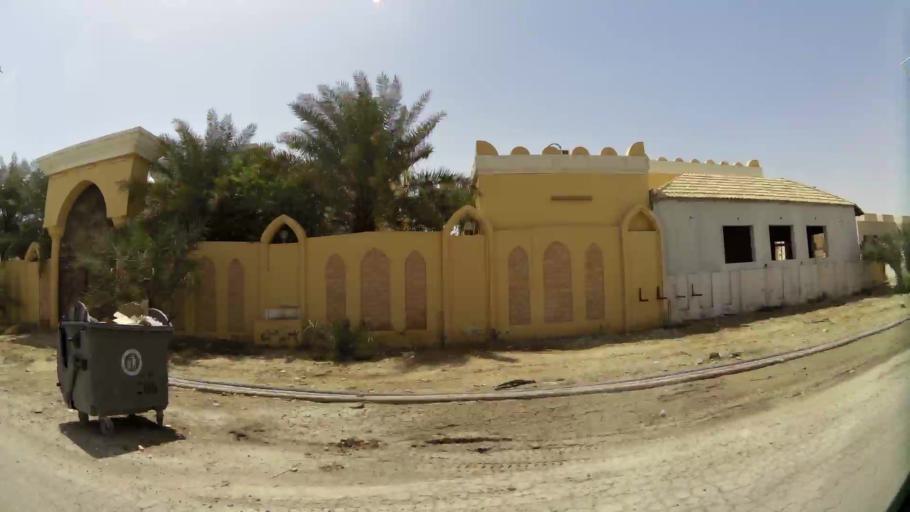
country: QA
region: Baladiyat Umm Salal
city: Umm Salal Muhammad
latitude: 25.3752
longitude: 51.4477
